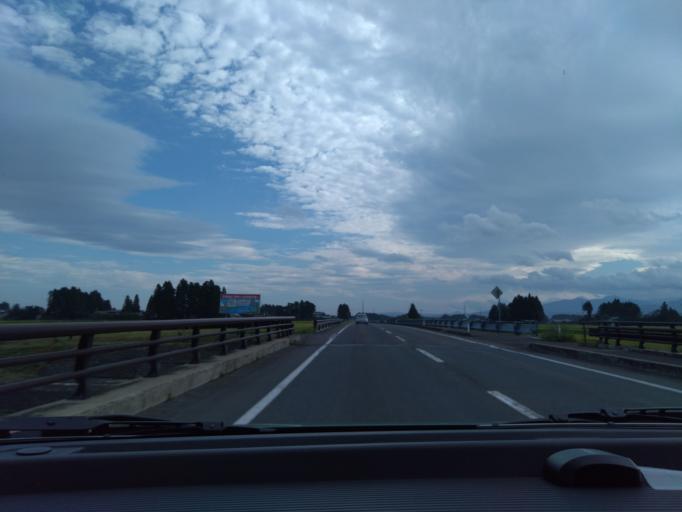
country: JP
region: Iwate
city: Hanamaki
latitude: 39.3523
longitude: 141.0537
